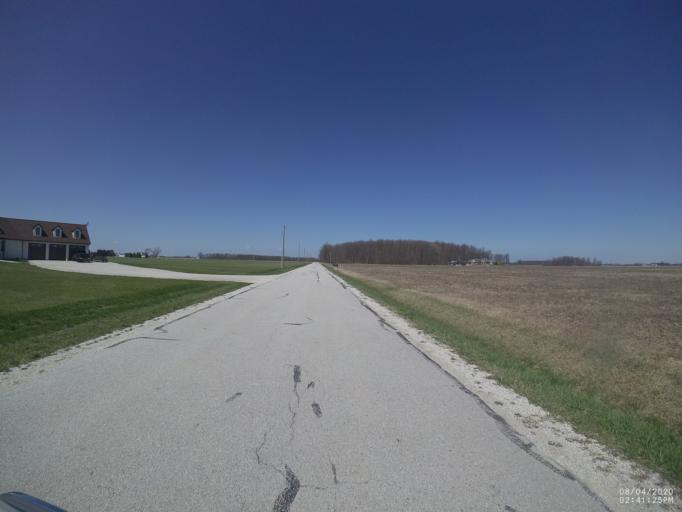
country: US
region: Ohio
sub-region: Sandusky County
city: Gibsonburg
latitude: 41.2861
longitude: -83.2969
